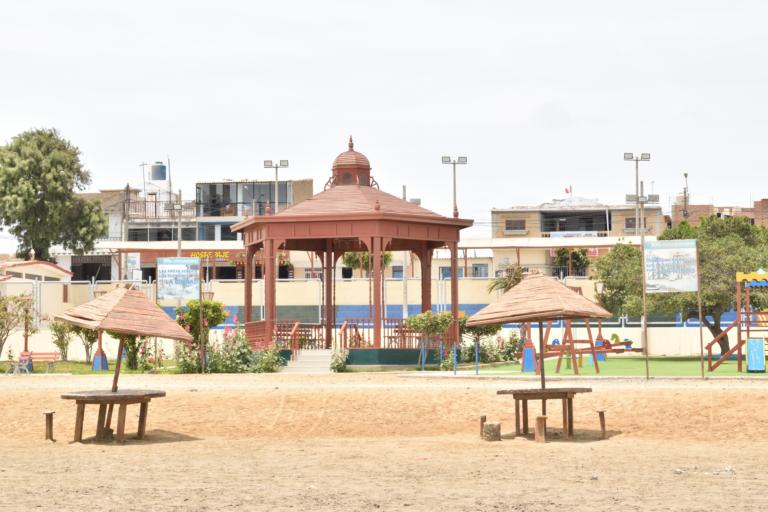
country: PE
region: La Libertad
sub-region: Ascope
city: Paijan
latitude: -7.7005
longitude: -79.4386
